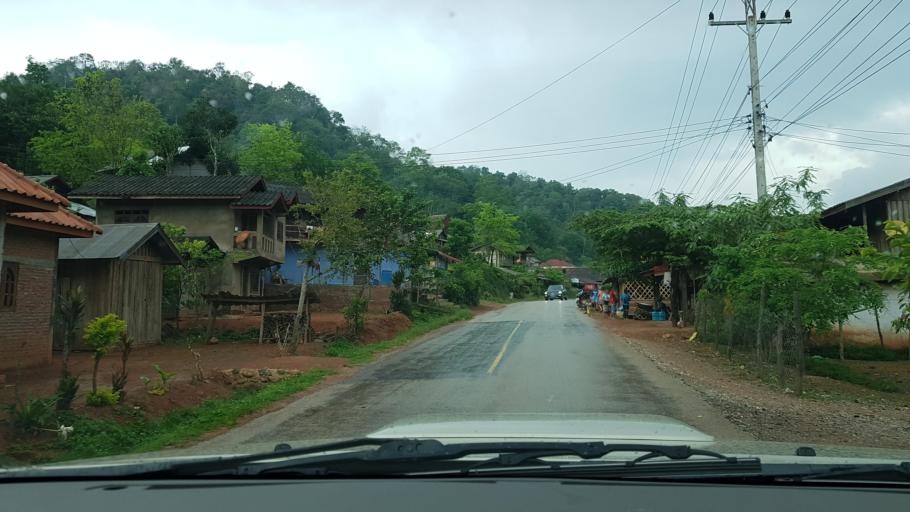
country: LA
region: Oudomxai
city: Muang Xay
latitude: 20.5915
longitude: 101.9336
